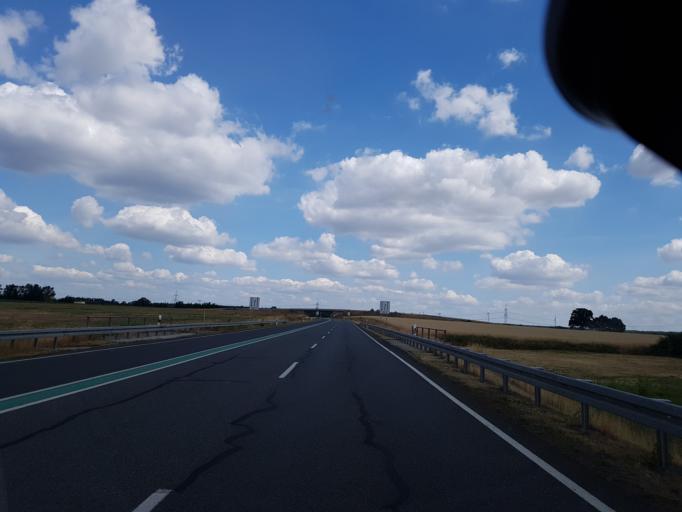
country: DE
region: Brandenburg
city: Drebkau
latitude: 51.6500
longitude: 14.2410
